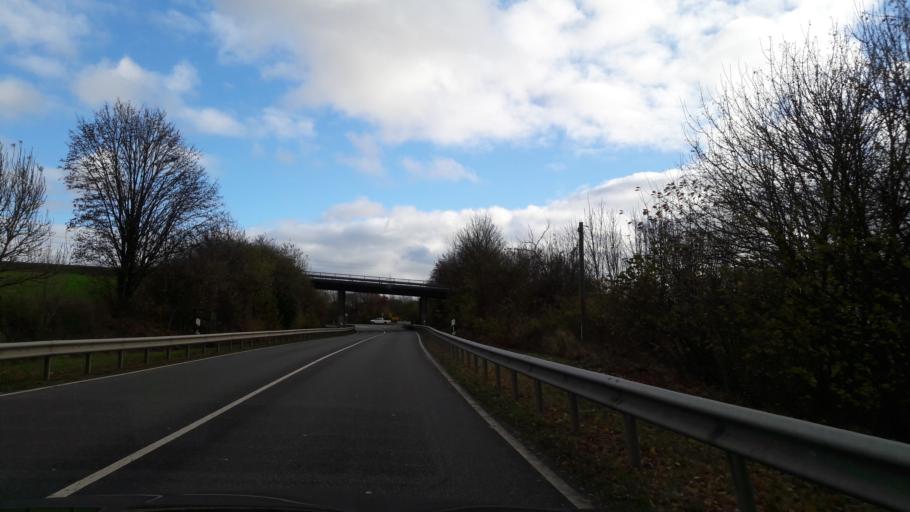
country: DE
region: Rheinland-Pfalz
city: Newel
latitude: 49.8179
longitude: 6.5547
